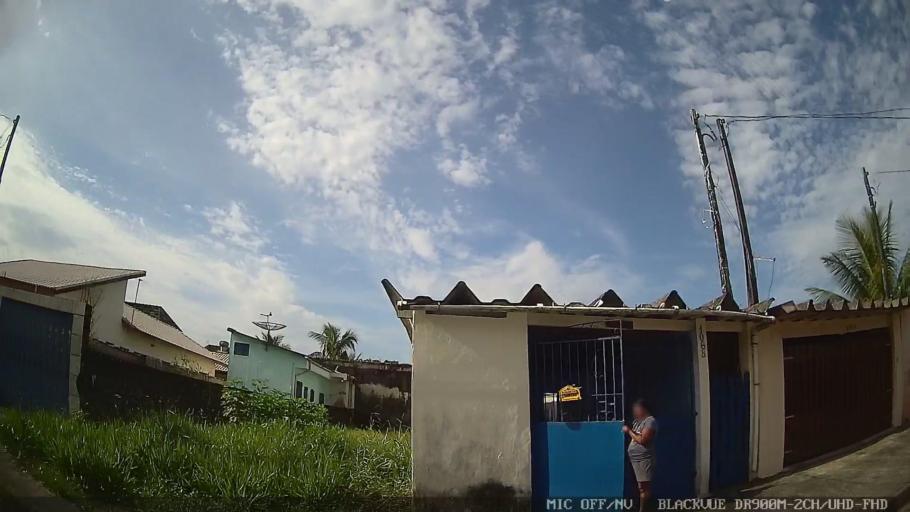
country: BR
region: Sao Paulo
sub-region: Itanhaem
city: Itanhaem
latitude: -24.1599
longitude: -46.7692
